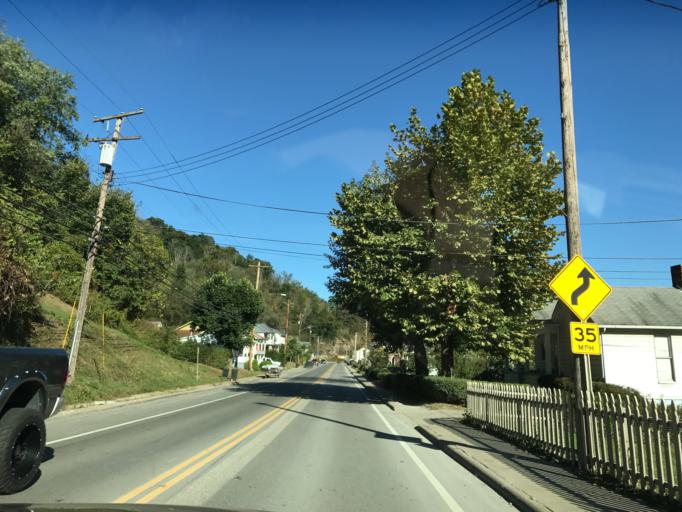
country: US
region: Ohio
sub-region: Belmont County
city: Wolfhurst
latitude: 40.0670
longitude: -80.8143
